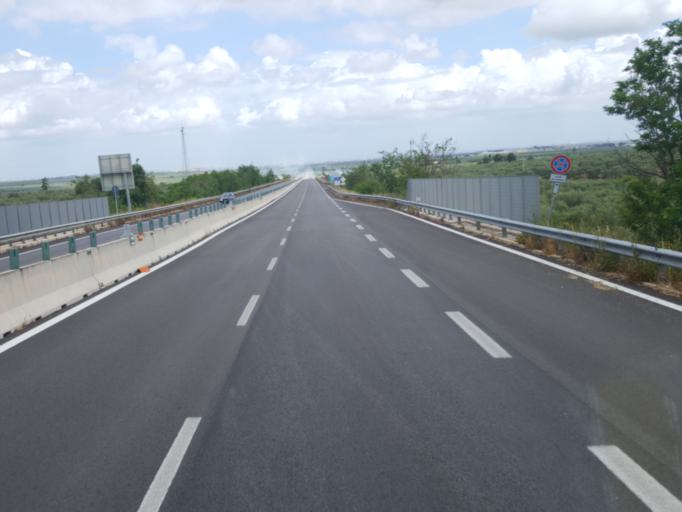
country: IT
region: Apulia
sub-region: Provincia di Bari
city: Toritto
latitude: 40.9976
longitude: 16.6643
